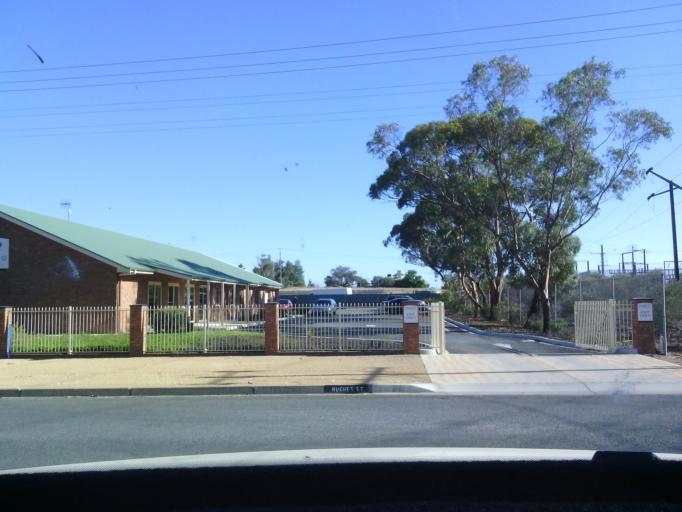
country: AU
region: South Australia
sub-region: Berri and Barmera
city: Berri
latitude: -34.2715
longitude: 140.5968
